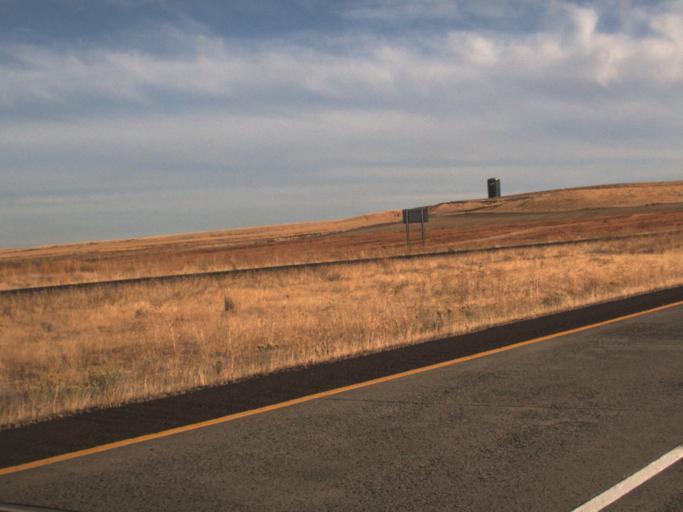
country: US
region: Washington
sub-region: Franklin County
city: Connell
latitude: 46.6800
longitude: -118.8426
